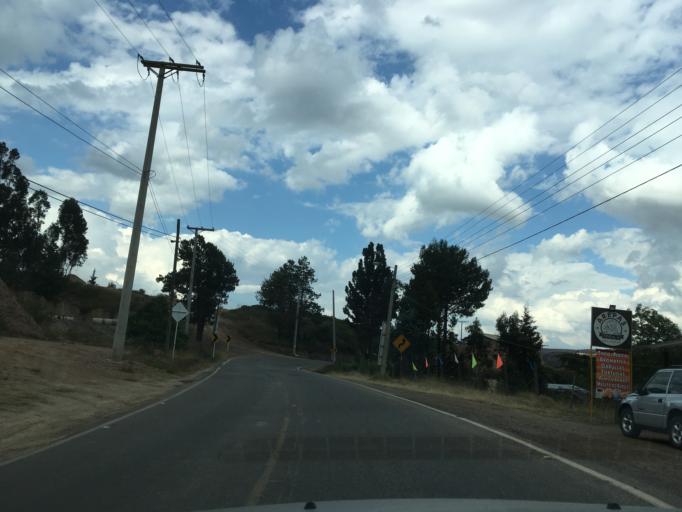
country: CO
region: Boyaca
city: Raquira
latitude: 5.5744
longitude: -73.6487
